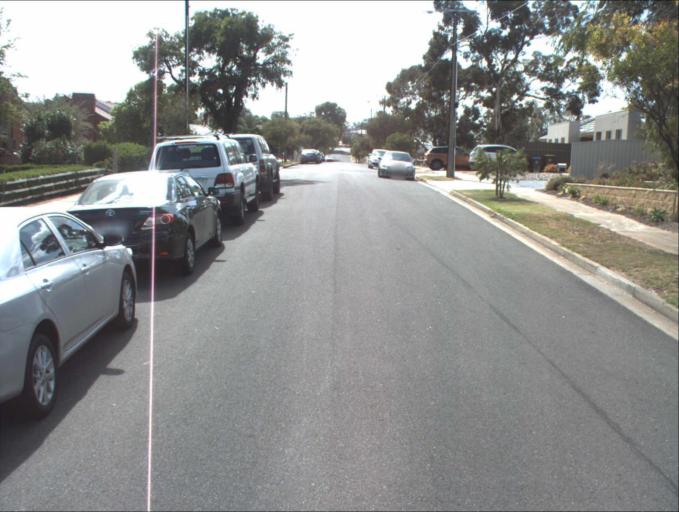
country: AU
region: South Australia
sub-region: Port Adelaide Enfield
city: Blair Athol
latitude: -34.8601
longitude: 138.5976
